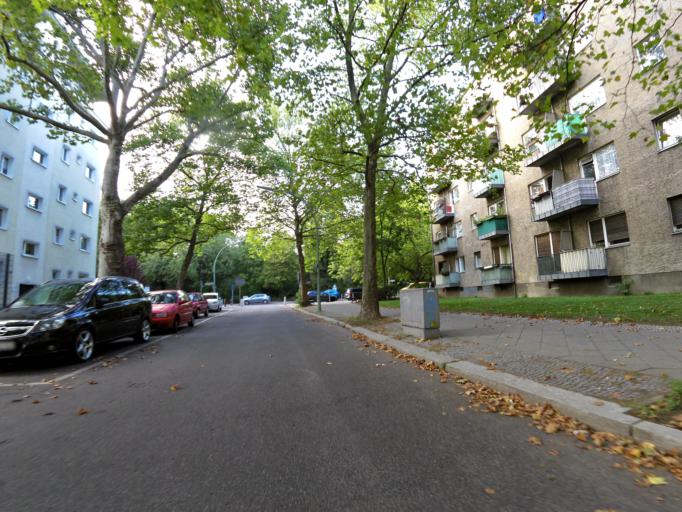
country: DE
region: Berlin
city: Berlin Schoeneberg
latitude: 52.4811
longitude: 13.3396
